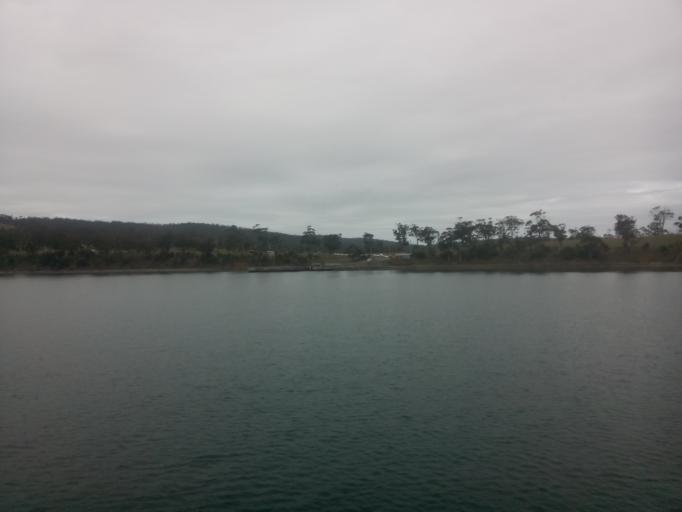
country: AU
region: Tasmania
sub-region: Kingborough
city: Kettering
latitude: -43.1405
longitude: 147.2839
